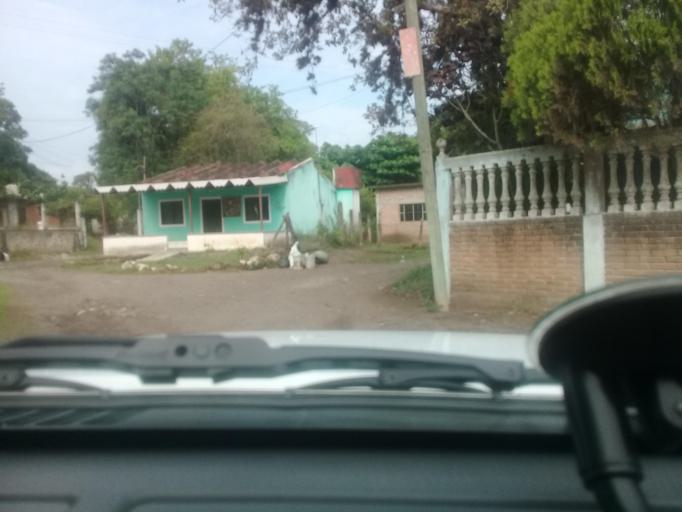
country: MX
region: Veracruz
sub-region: Paso de Ovejas
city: Tolome
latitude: 19.2628
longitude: -96.4122
